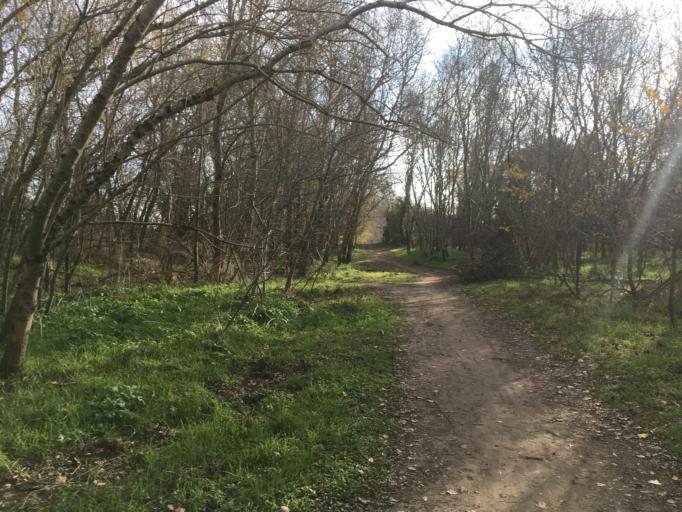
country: FR
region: Midi-Pyrenees
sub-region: Departement de la Haute-Garonne
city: Fenouillet
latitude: 43.6600
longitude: 1.4052
